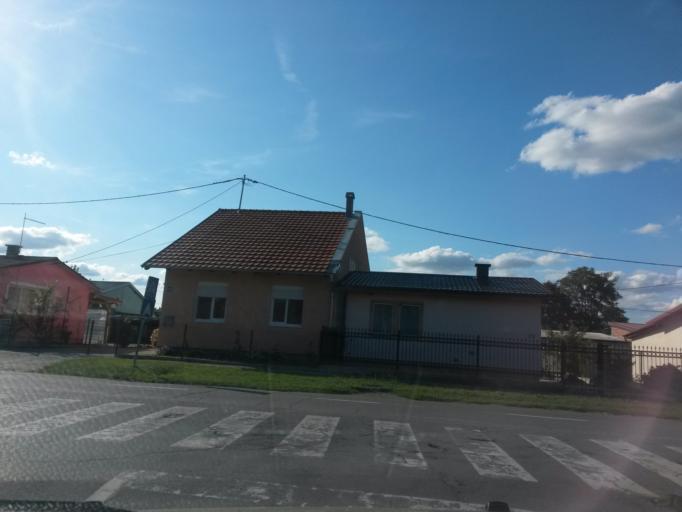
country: HR
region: Osjecko-Baranjska
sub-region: Grad Osijek
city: Osijek
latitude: 45.5461
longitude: 18.7214
